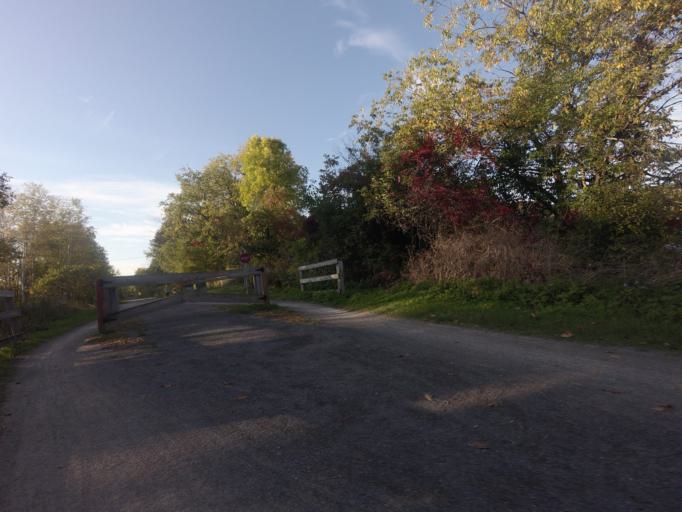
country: CA
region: Quebec
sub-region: Laurentides
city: Prevost
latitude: 45.8459
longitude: -74.0610
